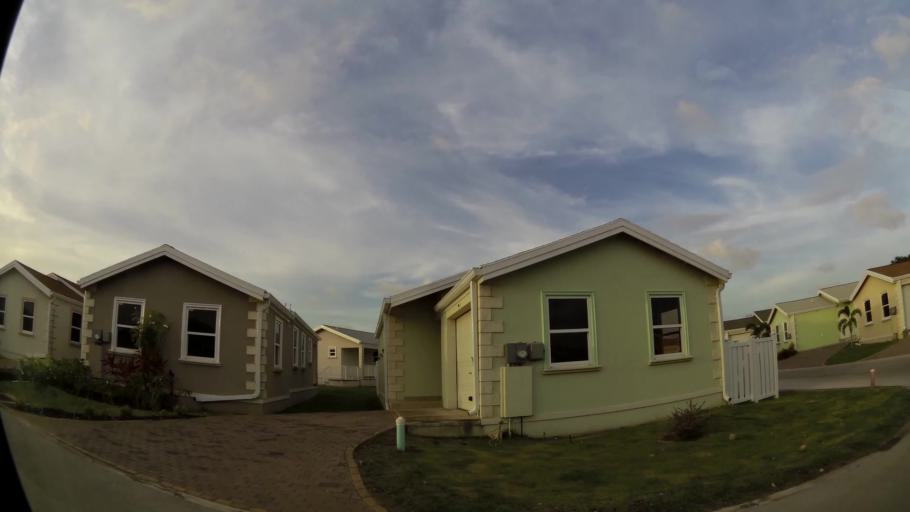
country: BB
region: Christ Church
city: Oistins
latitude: 13.0852
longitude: -59.4993
